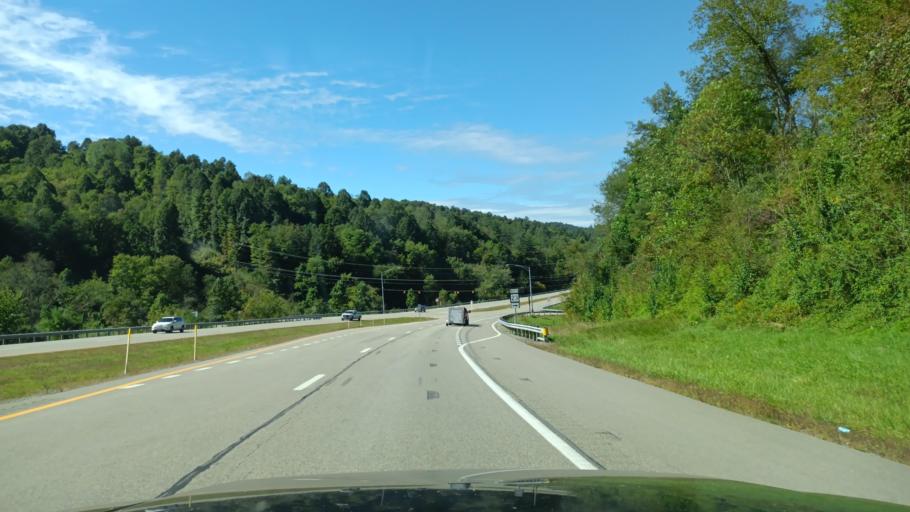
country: US
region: West Virginia
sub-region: Harrison County
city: Salem
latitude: 39.2939
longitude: -80.5657
